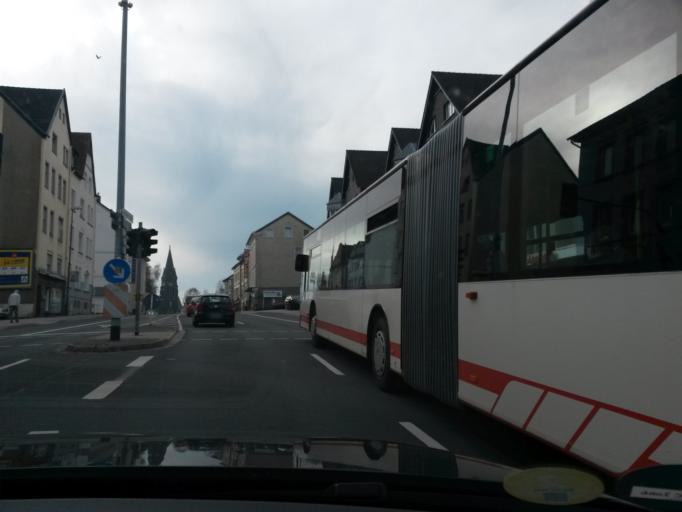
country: DE
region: North Rhine-Westphalia
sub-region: Regierungsbezirk Arnsberg
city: Luedenscheid
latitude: 51.2237
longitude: 7.6183
